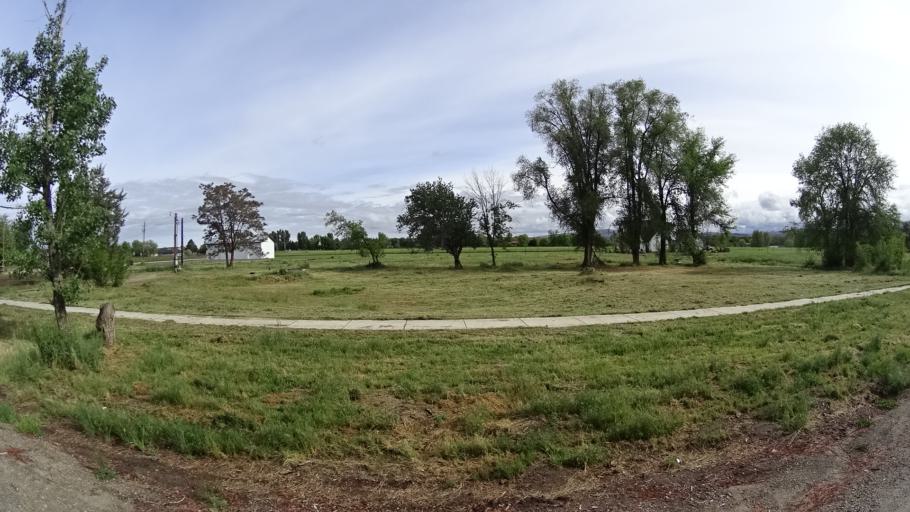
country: US
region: Idaho
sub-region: Ada County
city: Eagle
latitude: 43.7208
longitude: -116.3780
